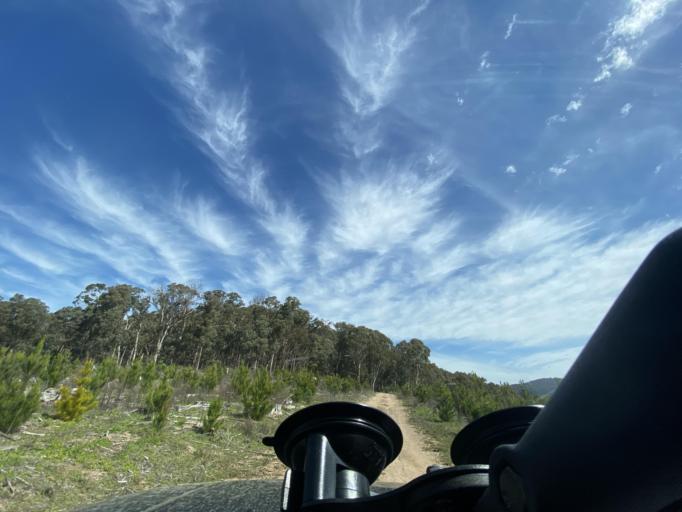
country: AU
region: Victoria
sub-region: Mansfield
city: Mansfield
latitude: -36.8320
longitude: 146.1015
